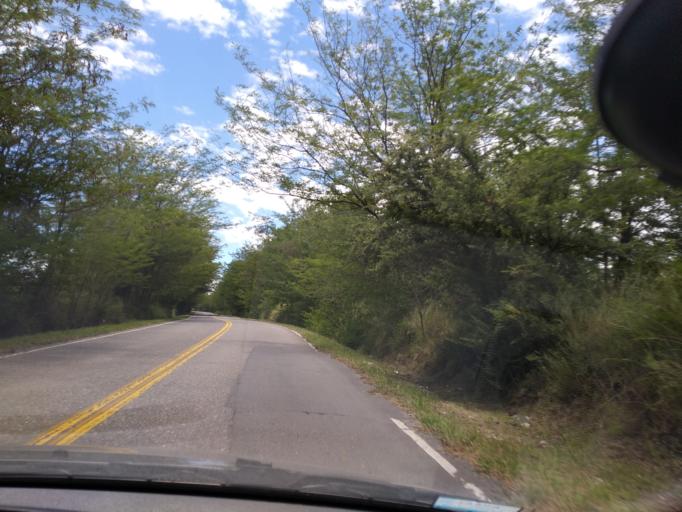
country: AR
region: Cordoba
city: Cuesta Blanca
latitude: -31.5949
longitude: -64.5652
